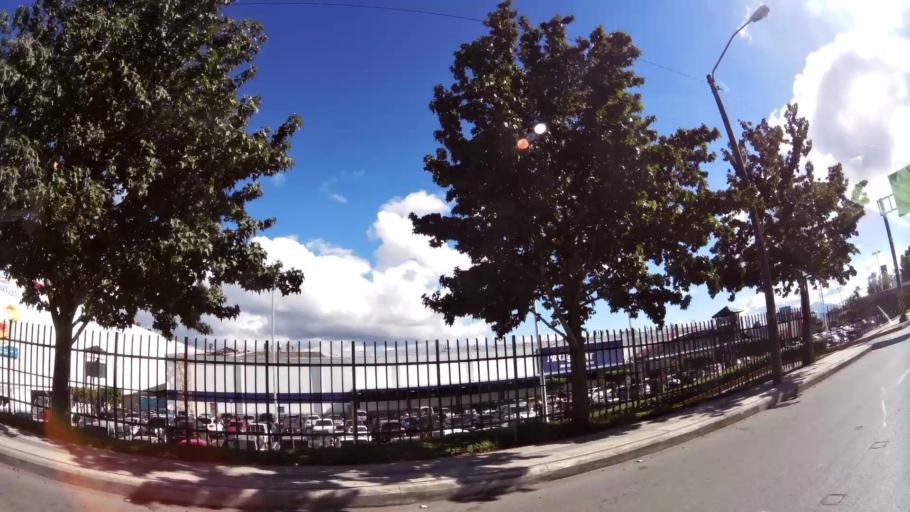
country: GT
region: Guatemala
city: Guatemala City
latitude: 14.6198
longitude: -90.5552
